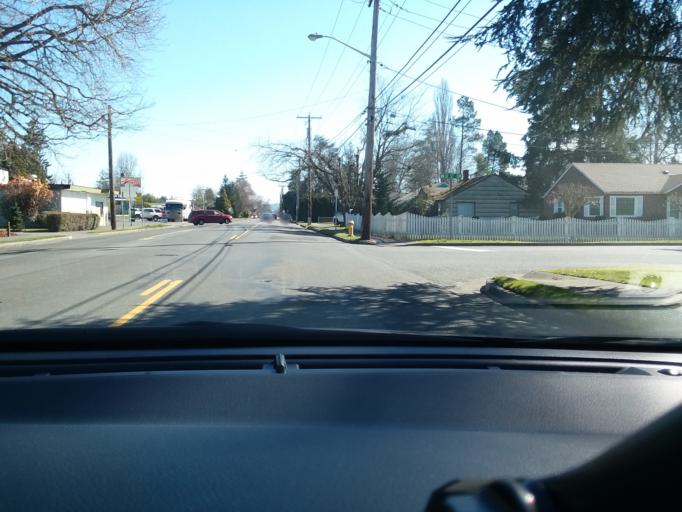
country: US
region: Washington
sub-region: Pierce County
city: Puyallup
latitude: 47.1903
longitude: -122.3194
